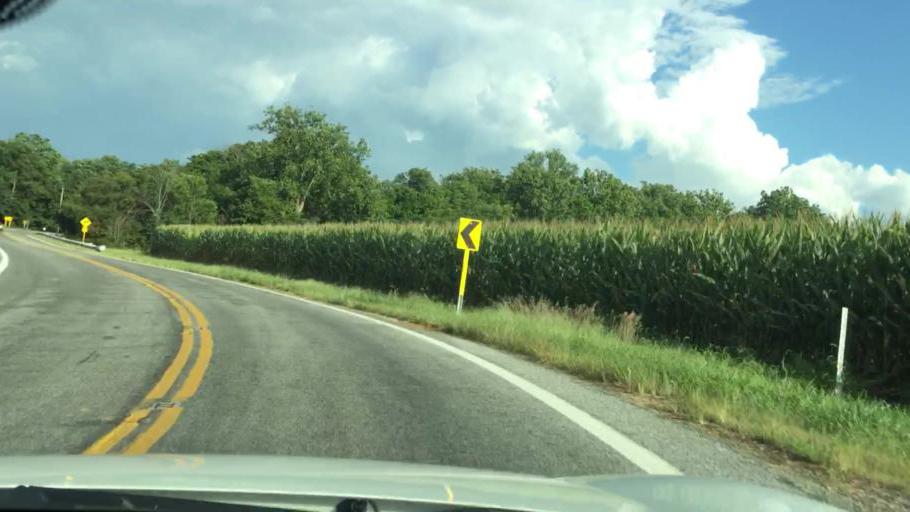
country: US
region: Ohio
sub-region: Champaign County
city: Mechanicsburg
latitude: 40.0417
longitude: -83.6076
